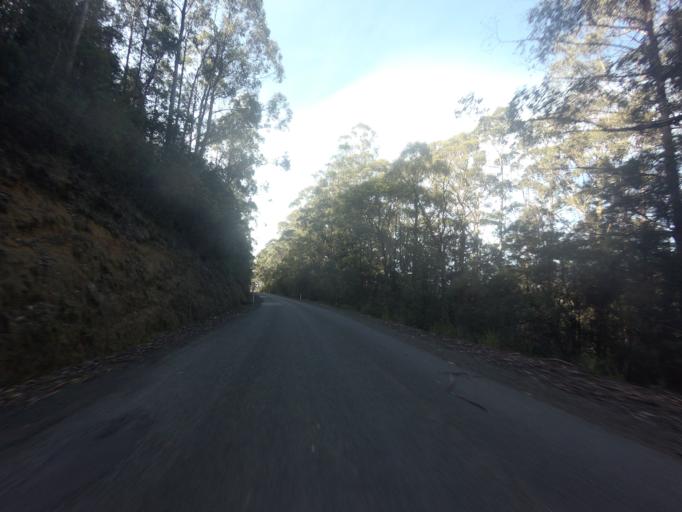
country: AU
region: Tasmania
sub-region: Kingborough
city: Kettering
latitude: -43.1704
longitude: 147.2010
